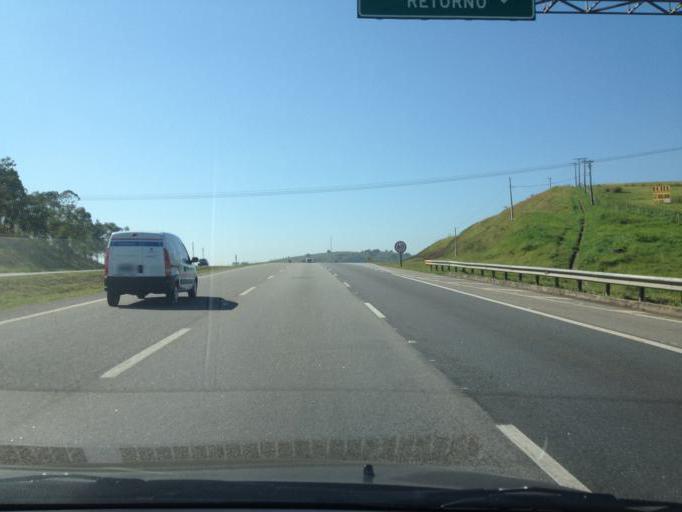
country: BR
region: Sao Paulo
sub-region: Guararema
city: Guararema
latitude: -23.3560
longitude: -46.0598
